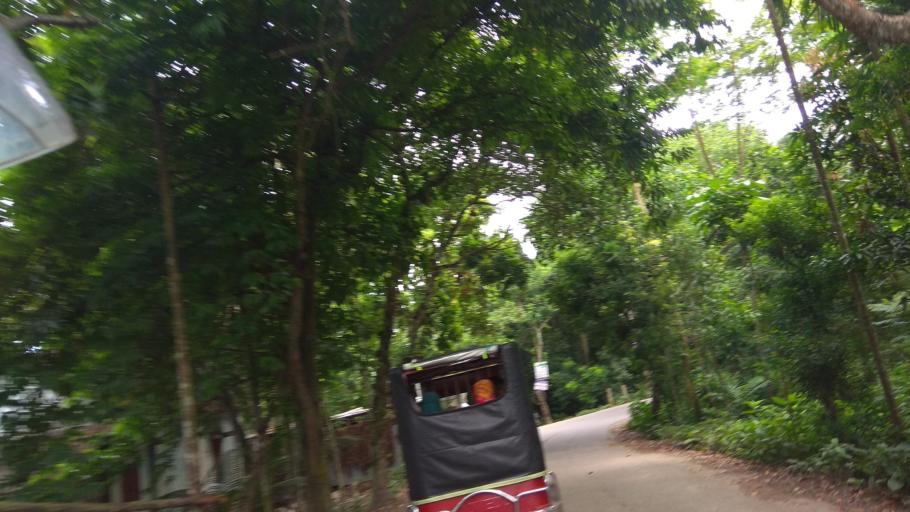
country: BD
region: Khulna
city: Kalia
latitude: 23.1638
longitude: 89.6443
